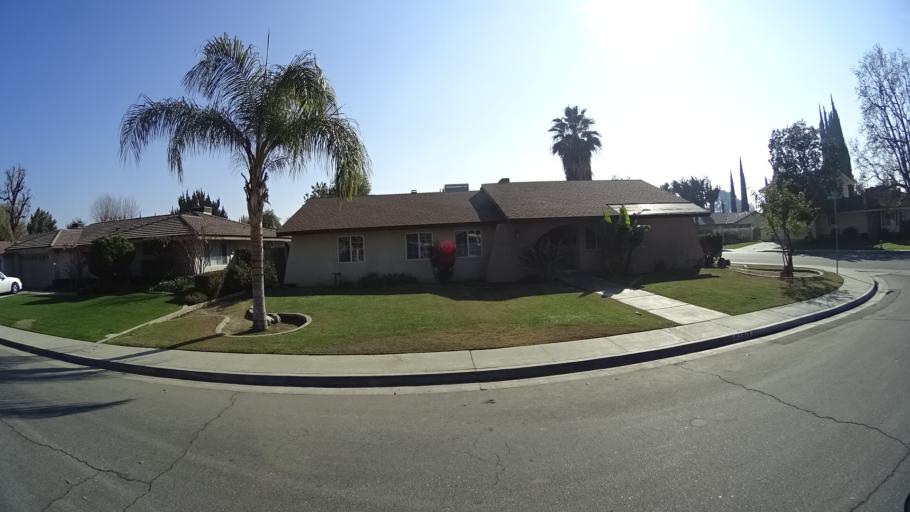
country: US
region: California
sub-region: Kern County
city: Greenacres
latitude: 35.3602
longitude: -119.0693
